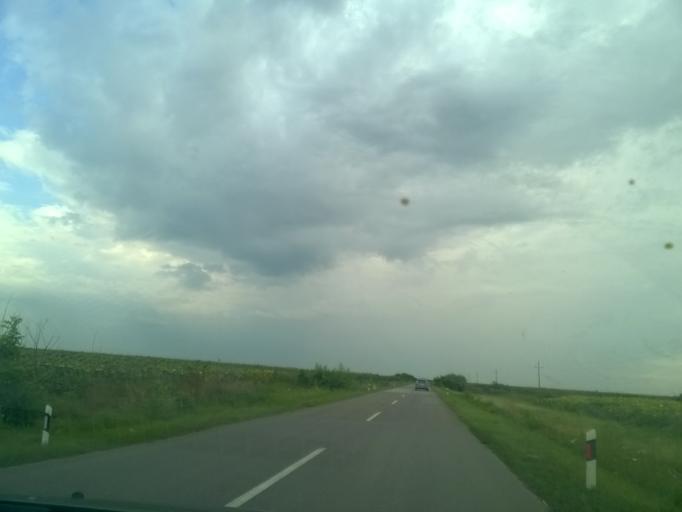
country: RS
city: Tomasevac
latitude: 45.2445
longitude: 20.6285
